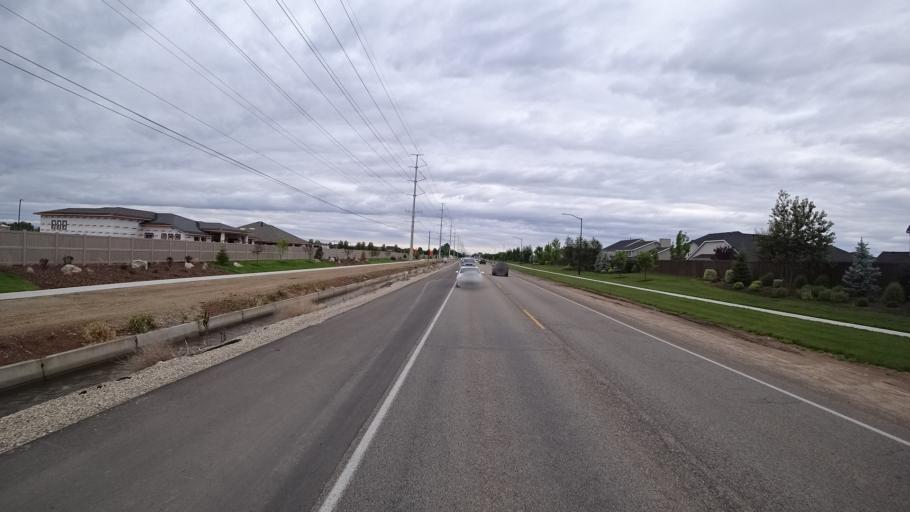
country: US
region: Idaho
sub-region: Ada County
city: Meridian
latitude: 43.6483
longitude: -116.4041
